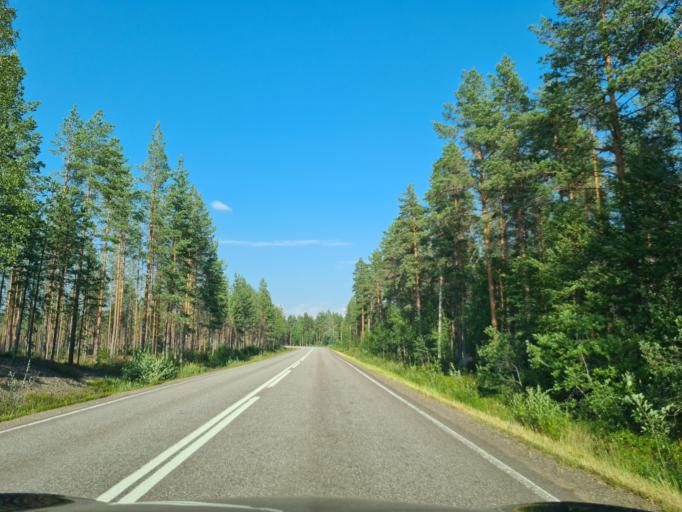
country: FI
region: Satakunta
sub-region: Pohjois-Satakunta
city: Karvia
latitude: 62.3232
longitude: 22.6768
